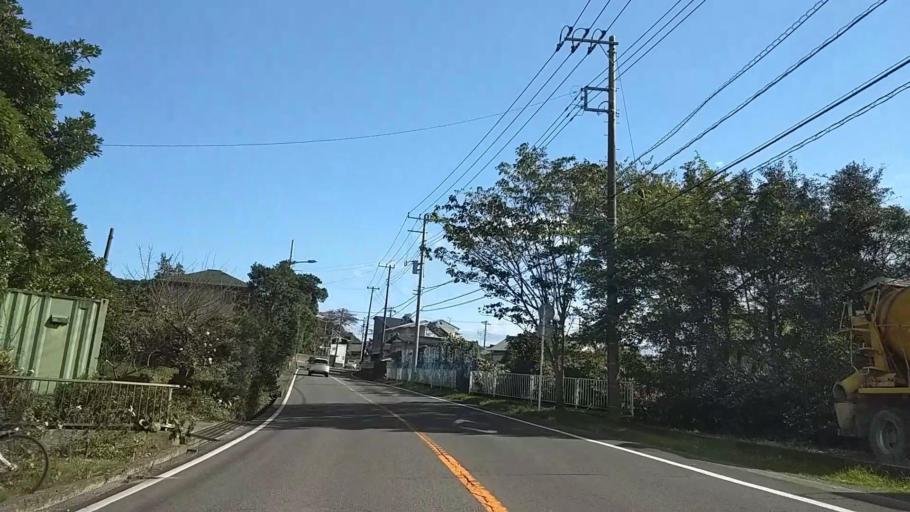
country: JP
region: Kanagawa
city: Odawara
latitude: 35.3158
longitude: 139.1725
